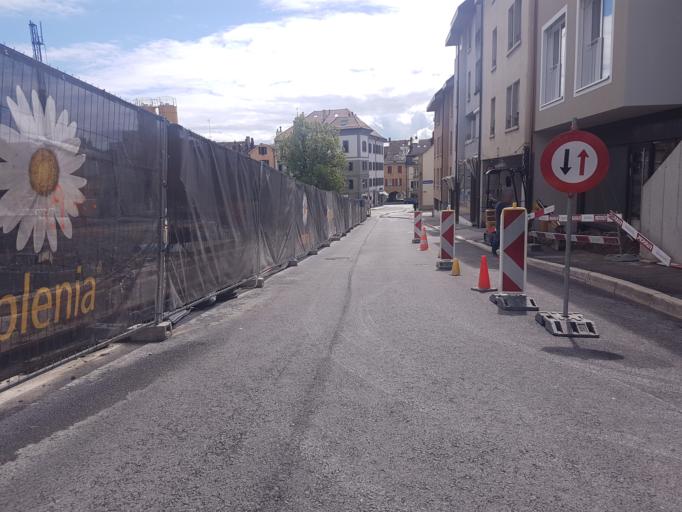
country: CH
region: Vaud
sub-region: Nyon District
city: Rolle
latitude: 46.4585
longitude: 6.3369
